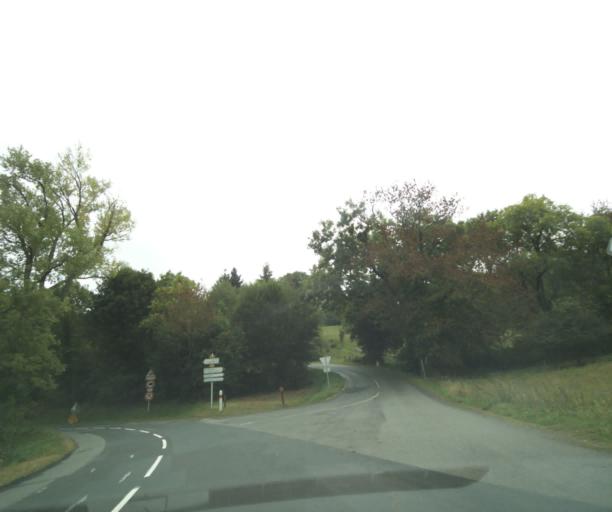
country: FR
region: Auvergne
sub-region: Departement du Puy-de-Dome
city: Orcines
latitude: 45.7677
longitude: 3.0140
